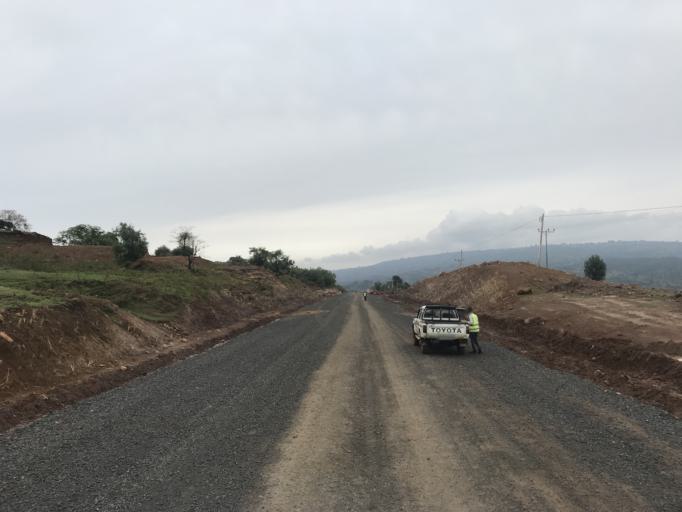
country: ET
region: Oromiya
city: Shambu
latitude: 10.0749
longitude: 36.8796
